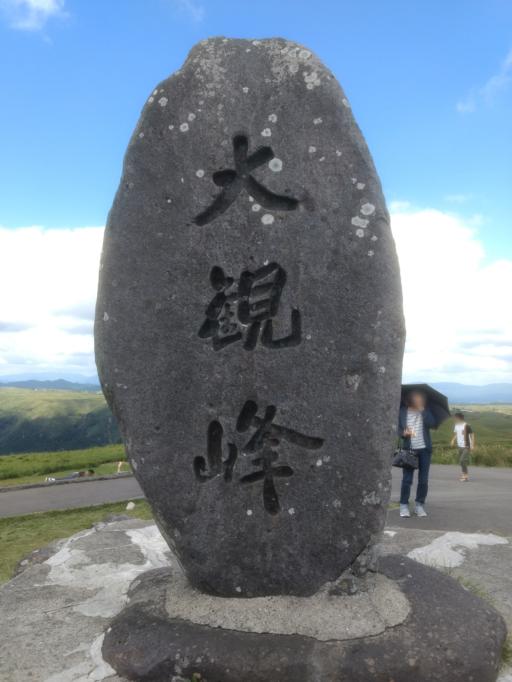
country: JP
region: Kumamoto
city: Aso
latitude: 32.9963
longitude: 131.0672
